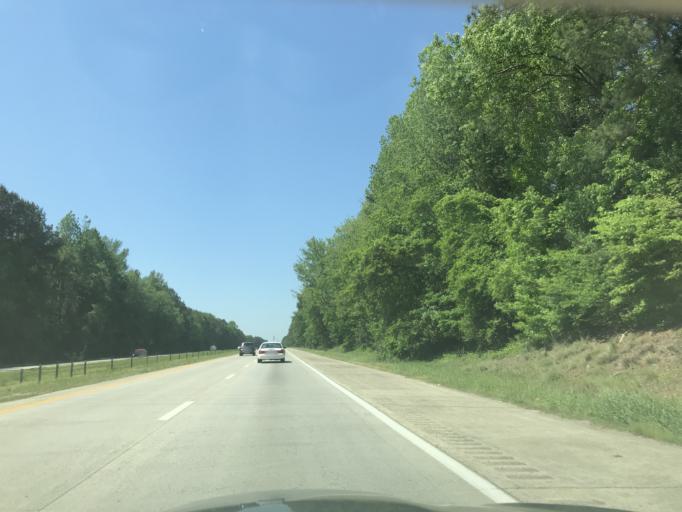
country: US
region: North Carolina
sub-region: Johnston County
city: Benson
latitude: 35.5322
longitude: -78.5690
